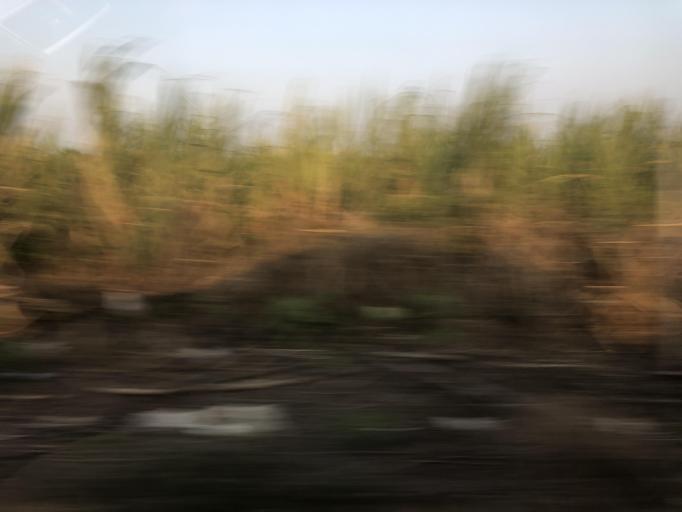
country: TW
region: Taiwan
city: Xinying
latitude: 23.1622
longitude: 120.2708
